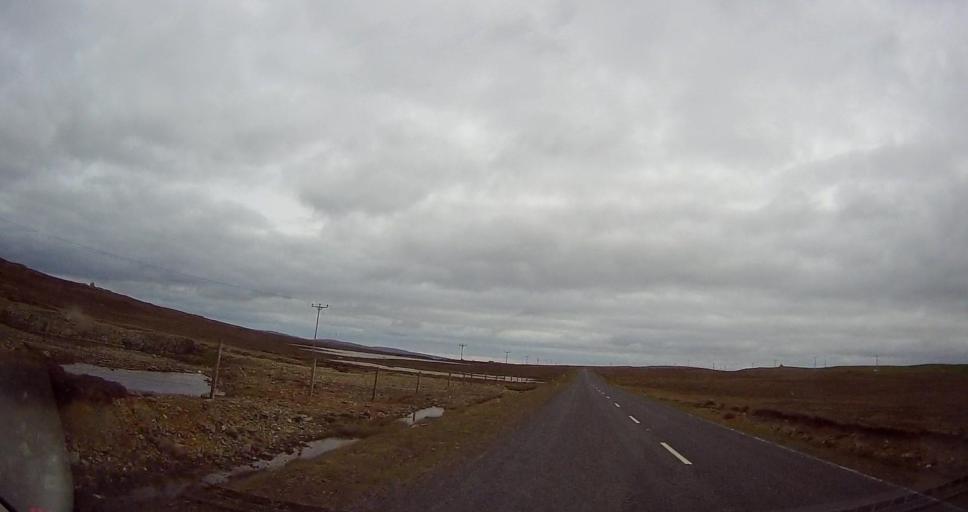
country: GB
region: Scotland
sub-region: Shetland Islands
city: Shetland
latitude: 60.7172
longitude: -0.9130
